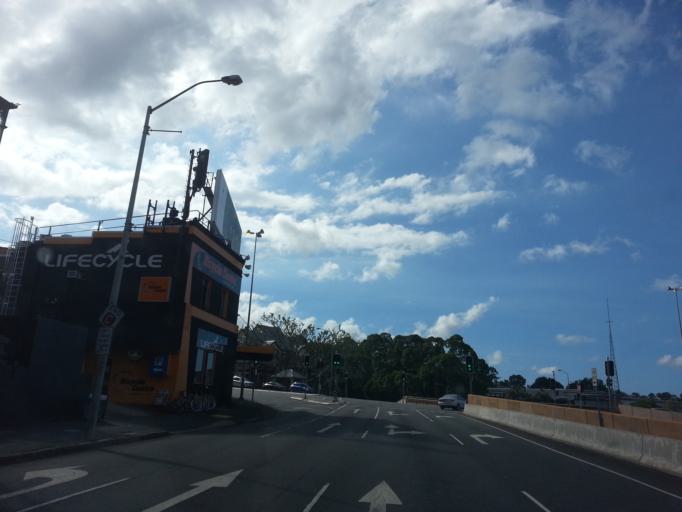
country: AU
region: Queensland
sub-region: Brisbane
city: Spring Hill
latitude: -27.4605
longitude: 153.0146
